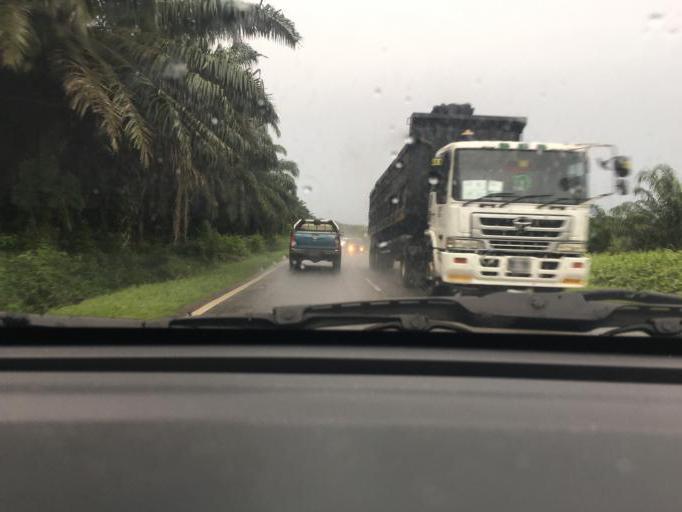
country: MY
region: Kedah
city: Bedong
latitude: 5.6579
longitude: 100.6317
